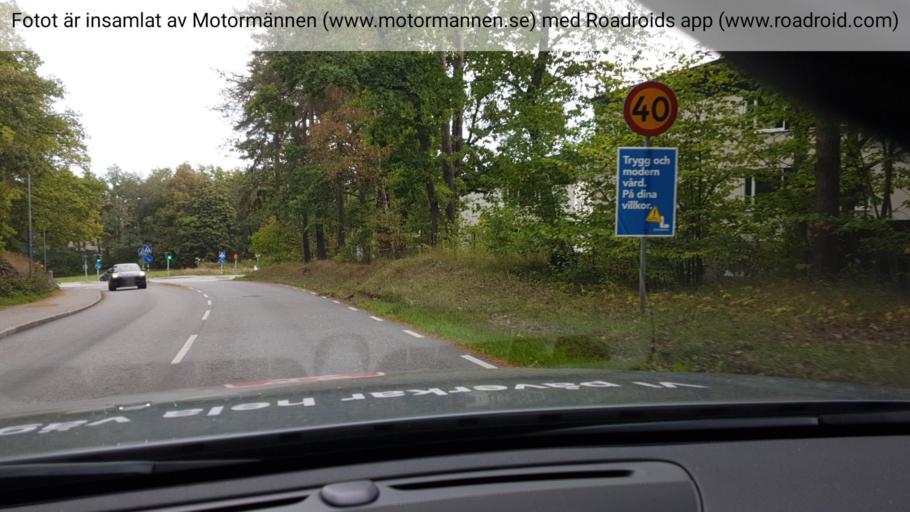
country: SE
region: Stockholm
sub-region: Danderyds Kommun
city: Djursholm
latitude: 59.3860
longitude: 18.0671
